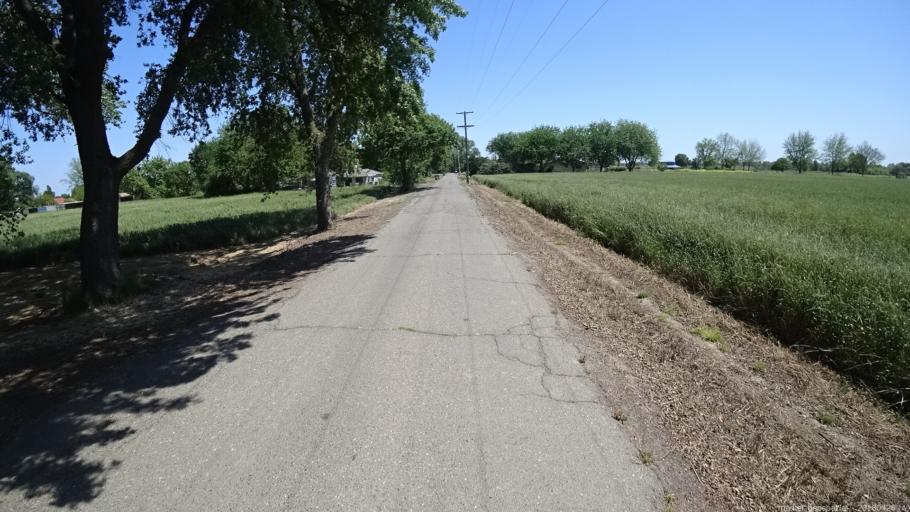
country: US
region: California
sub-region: Yolo County
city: West Sacramento
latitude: 38.5235
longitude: -121.5526
